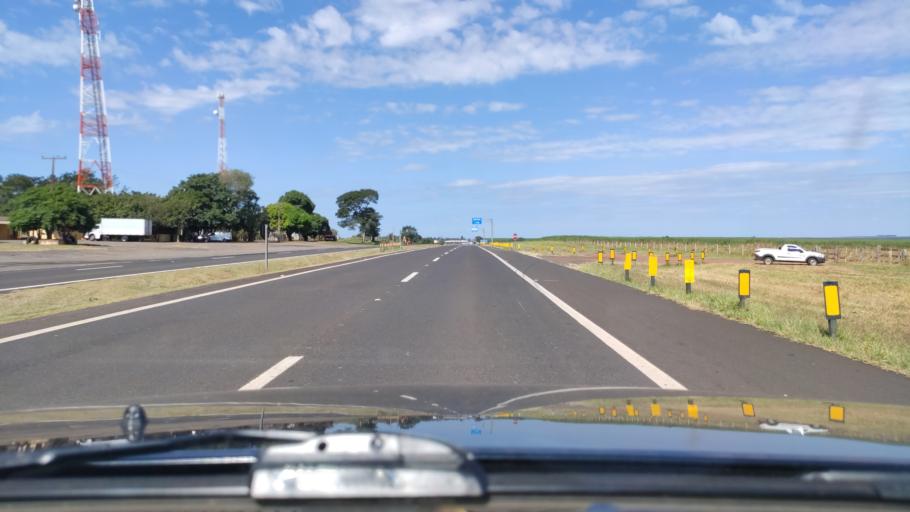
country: BR
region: Sao Paulo
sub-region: Rancharia
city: Rancharia
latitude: -22.4288
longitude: -51.0199
